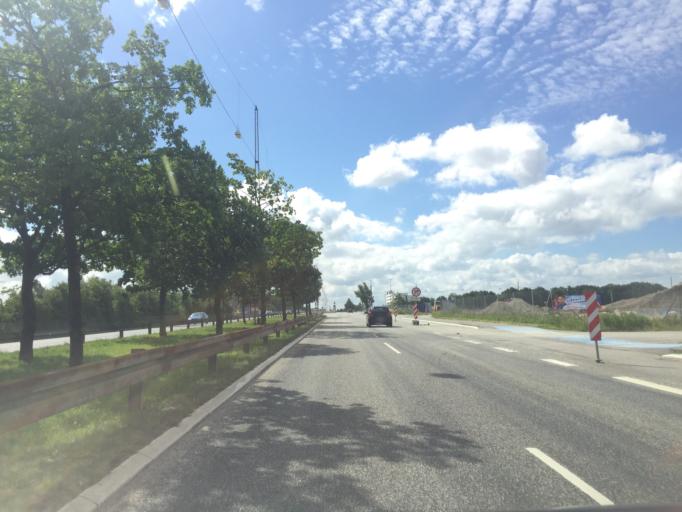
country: DK
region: Capital Region
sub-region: Hvidovre Kommune
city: Hvidovre
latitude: 55.6513
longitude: 12.4573
